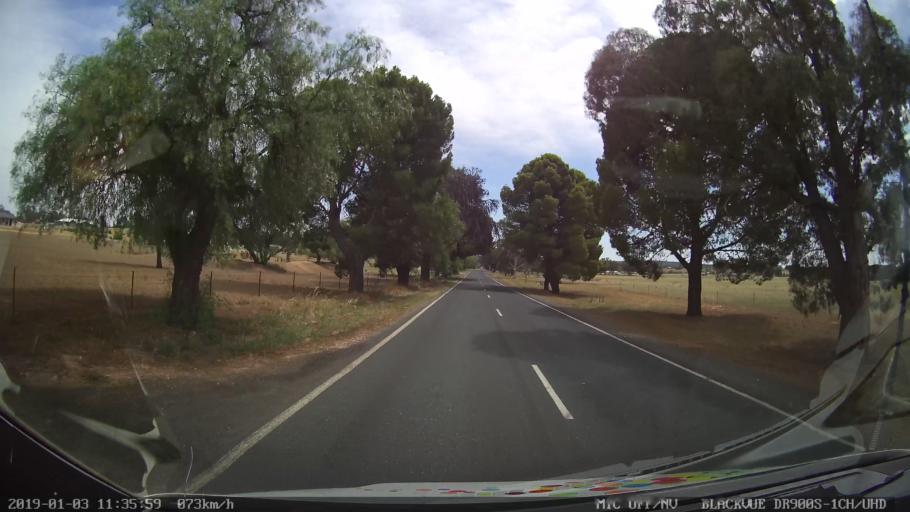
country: AU
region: New South Wales
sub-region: Weddin
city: Grenfell
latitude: -33.9160
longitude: 148.1594
